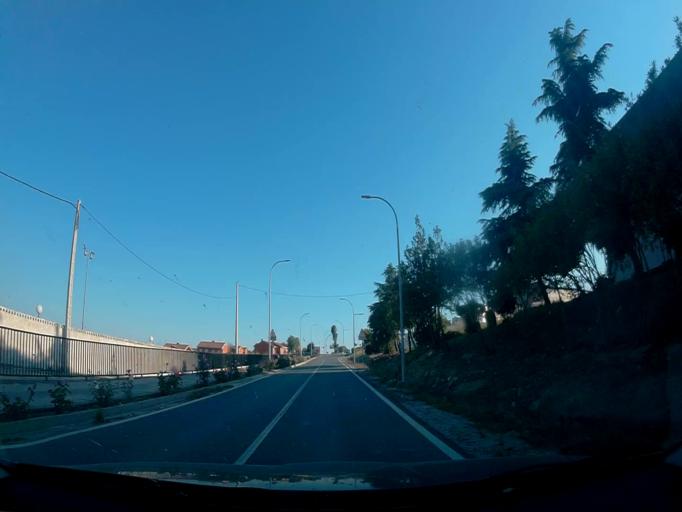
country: ES
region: Castille-La Mancha
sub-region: Province of Toledo
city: Almorox
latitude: 40.2277
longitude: -4.3926
